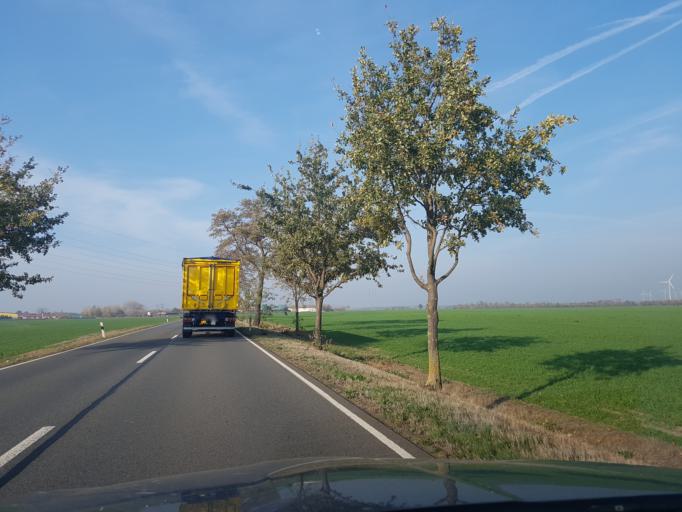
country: DE
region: Brandenburg
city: Bad Liebenwerda
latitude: 51.5295
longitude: 13.3168
